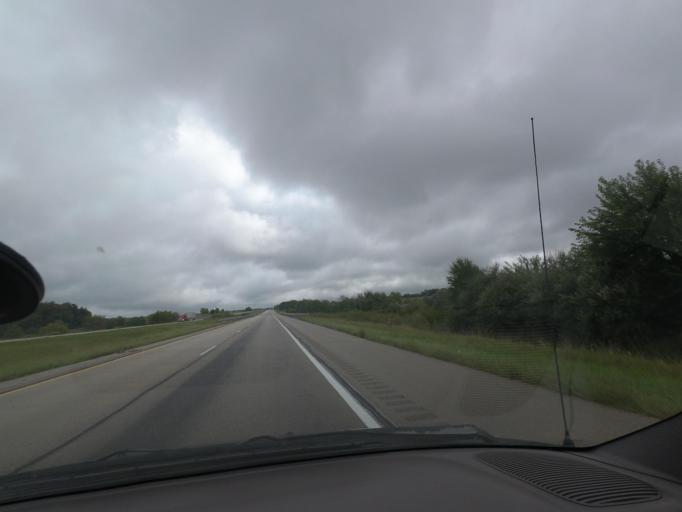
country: US
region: Illinois
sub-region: Piatt County
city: Monticello
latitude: 40.0308
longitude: -88.6252
